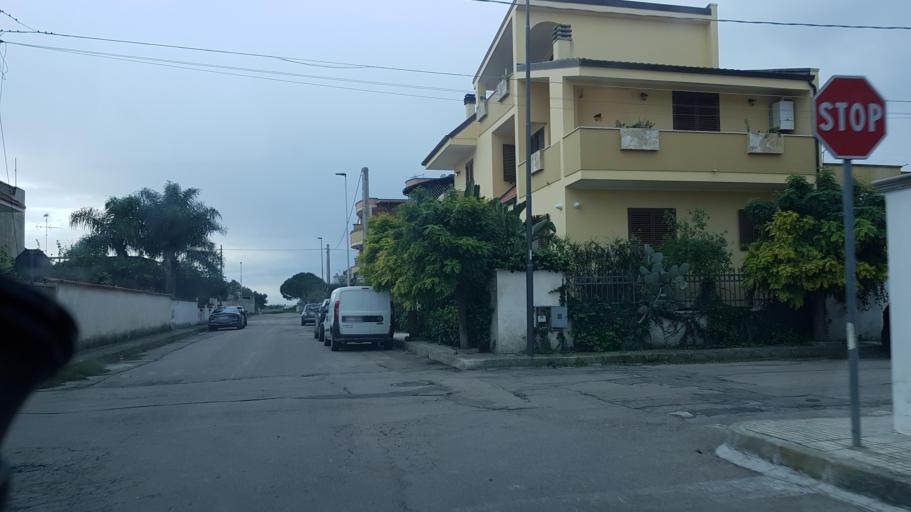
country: IT
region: Apulia
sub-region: Provincia di Lecce
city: Merine
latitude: 40.3321
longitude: 18.2211
